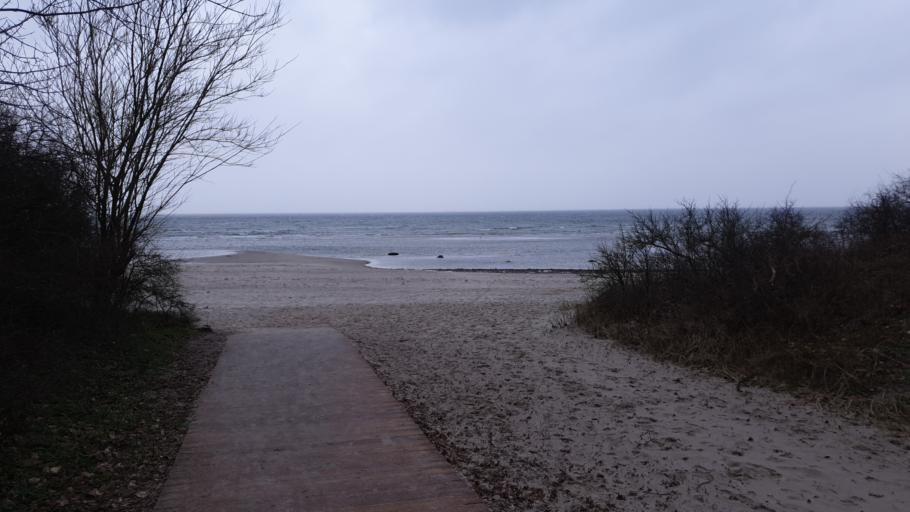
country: DE
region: Mecklenburg-Vorpommern
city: Kalkhorst
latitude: 53.9940
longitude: 11.0059
